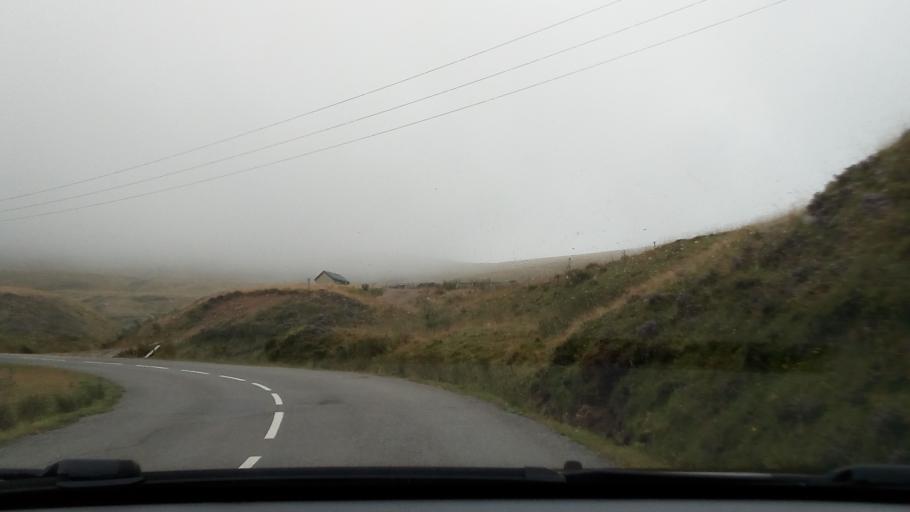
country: FR
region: Aquitaine
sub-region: Departement des Pyrenees-Atlantiques
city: Laruns
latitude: 42.9737
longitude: -0.3459
